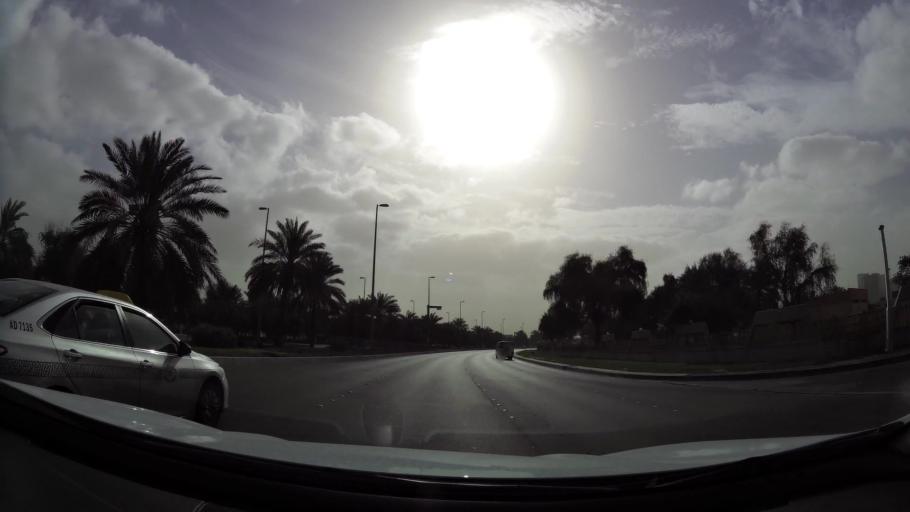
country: AE
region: Abu Dhabi
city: Abu Dhabi
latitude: 24.4323
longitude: 54.4397
